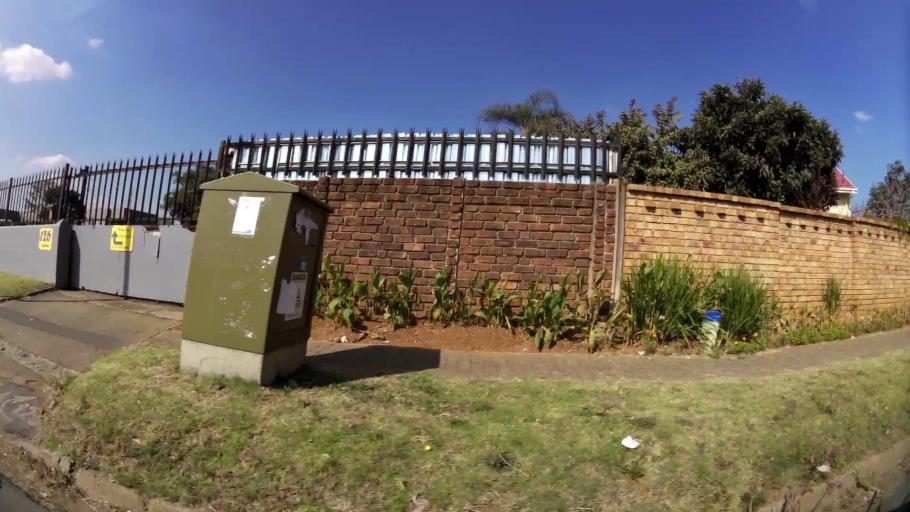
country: ZA
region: Gauteng
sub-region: City of Johannesburg Metropolitan Municipality
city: Modderfontein
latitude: -26.0843
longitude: 28.2409
